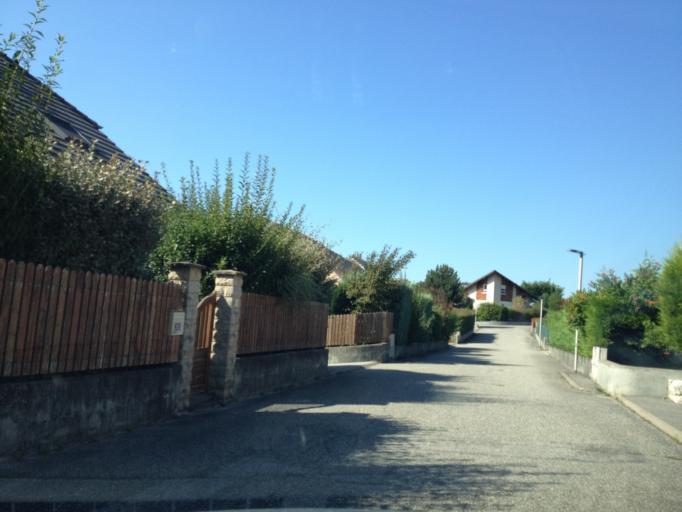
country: FR
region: Rhone-Alpes
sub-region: Departement de la Savoie
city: Jacob-Bellecombette
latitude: 45.5521
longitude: 5.9177
